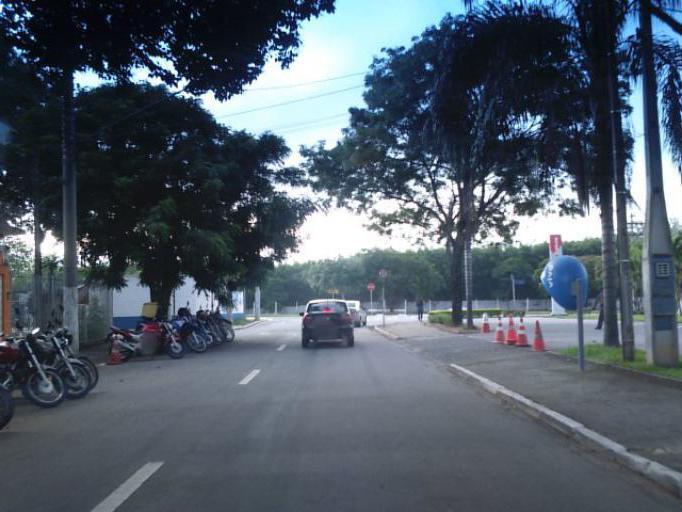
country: BR
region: Sao Paulo
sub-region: Sao Jose Dos Campos
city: Sao Jose dos Campos
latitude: -23.1950
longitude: -45.8733
